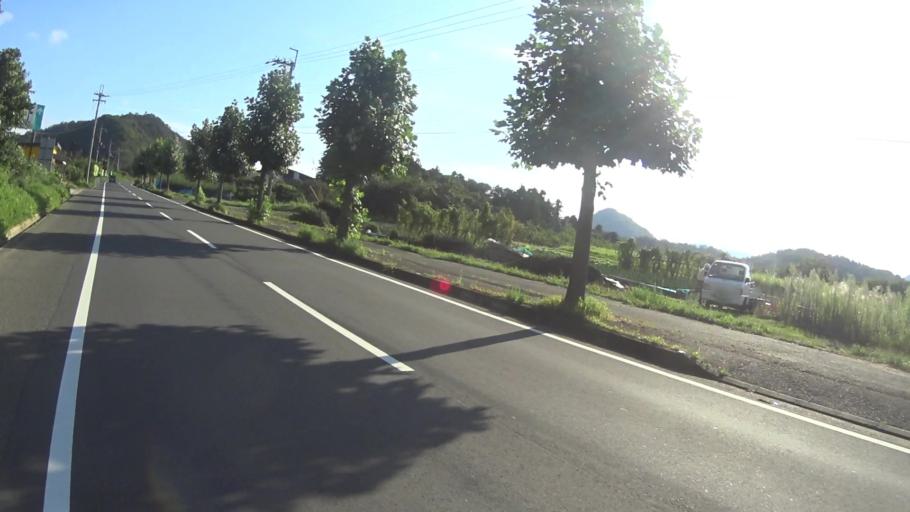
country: JP
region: Hyogo
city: Toyooka
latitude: 35.6249
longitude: 134.9285
